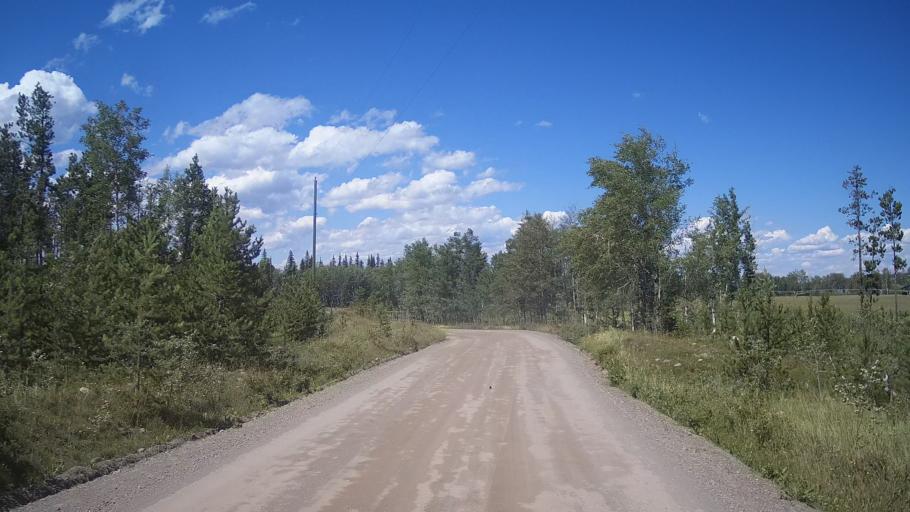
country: CA
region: British Columbia
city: Cache Creek
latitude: 51.2564
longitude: -121.6800
